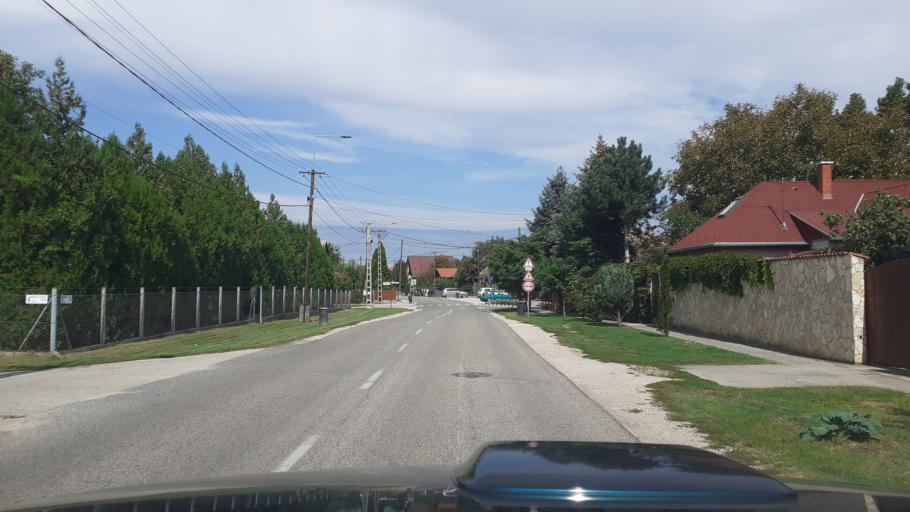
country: HU
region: Fejer
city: Pakozd
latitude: 47.1744
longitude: 18.5661
